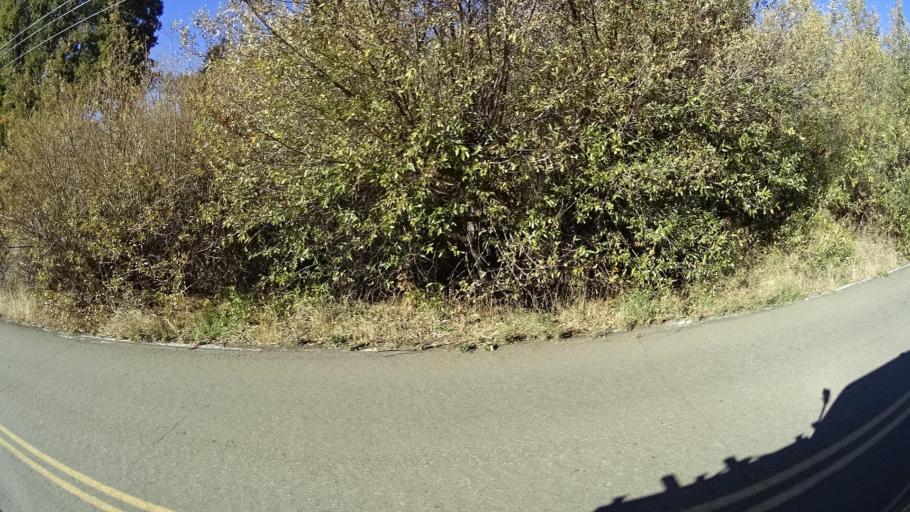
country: US
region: California
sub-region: Kern County
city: Alta Sierra
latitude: 35.7890
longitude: -118.7040
